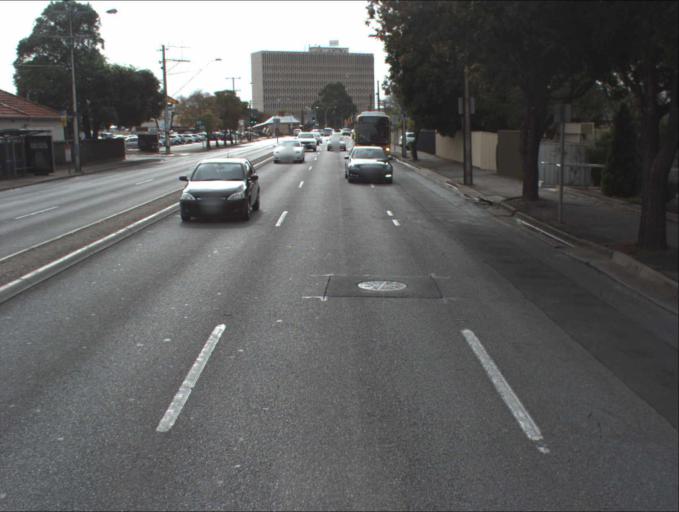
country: AU
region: South Australia
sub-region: Prospect
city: Prospect
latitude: -34.8915
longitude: 138.6111
